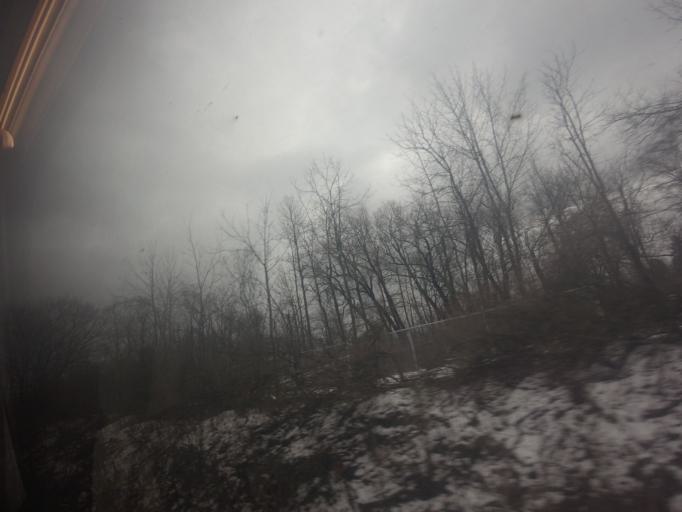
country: CA
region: Ontario
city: Cobourg
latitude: 43.9503
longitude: -78.2790
